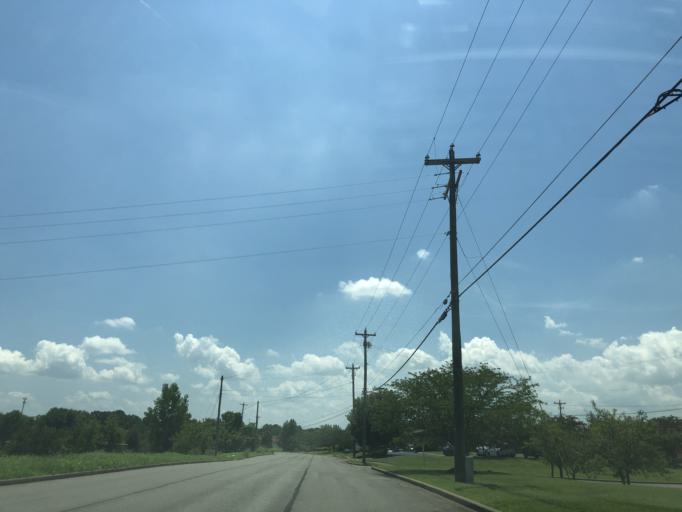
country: US
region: Tennessee
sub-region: Davidson County
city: Lakewood
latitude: 36.1820
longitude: -86.6365
